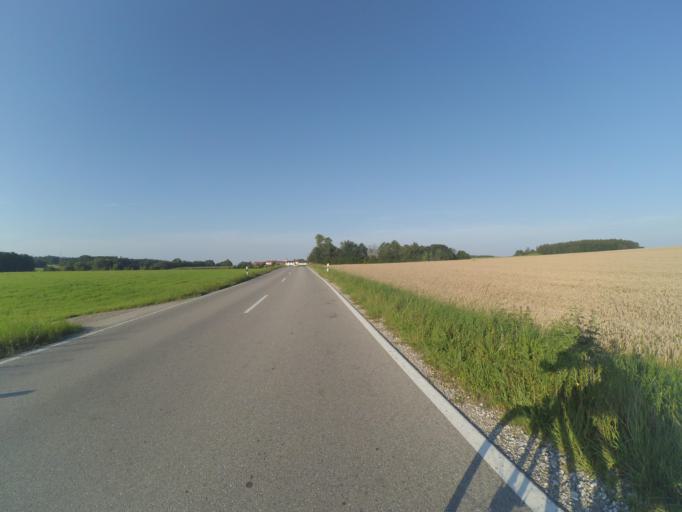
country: DE
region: Bavaria
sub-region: Swabia
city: Bad Worishofen
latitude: 48.0137
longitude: 10.5550
